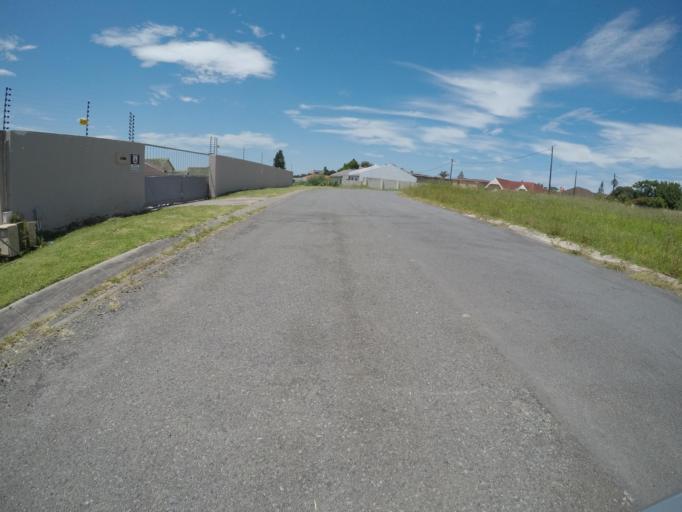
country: ZA
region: Eastern Cape
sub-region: Buffalo City Metropolitan Municipality
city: East London
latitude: -33.0318
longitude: 27.8534
